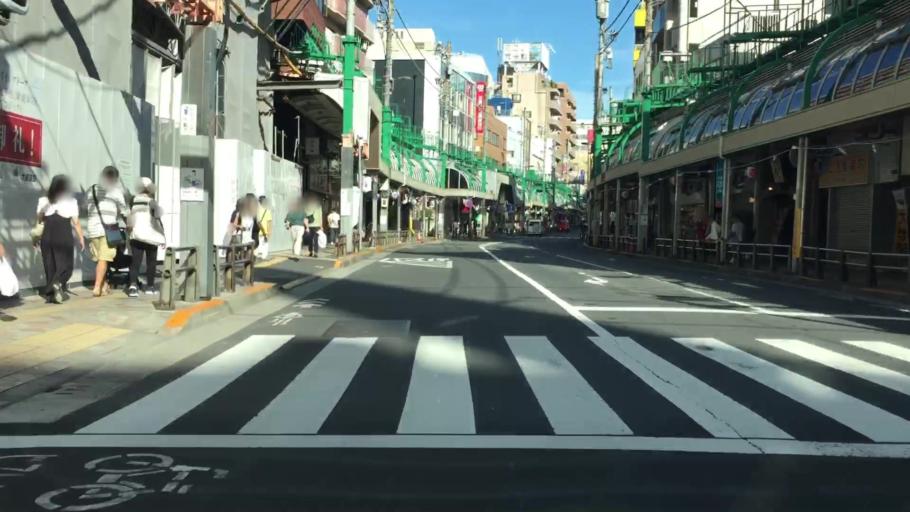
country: JP
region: Saitama
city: Soka
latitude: 35.7507
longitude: 139.8009
